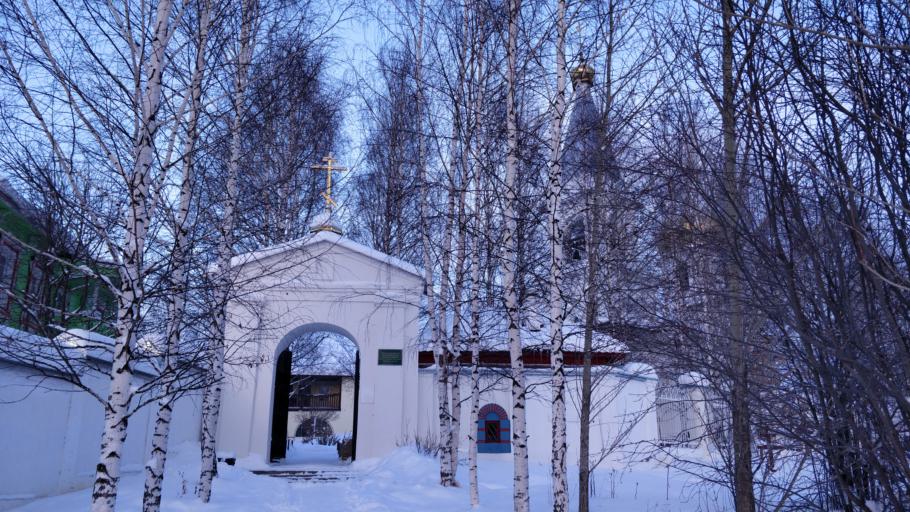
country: RU
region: Perm
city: Verkhnechusovskiye Gorodki
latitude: 58.1975
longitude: 57.1389
